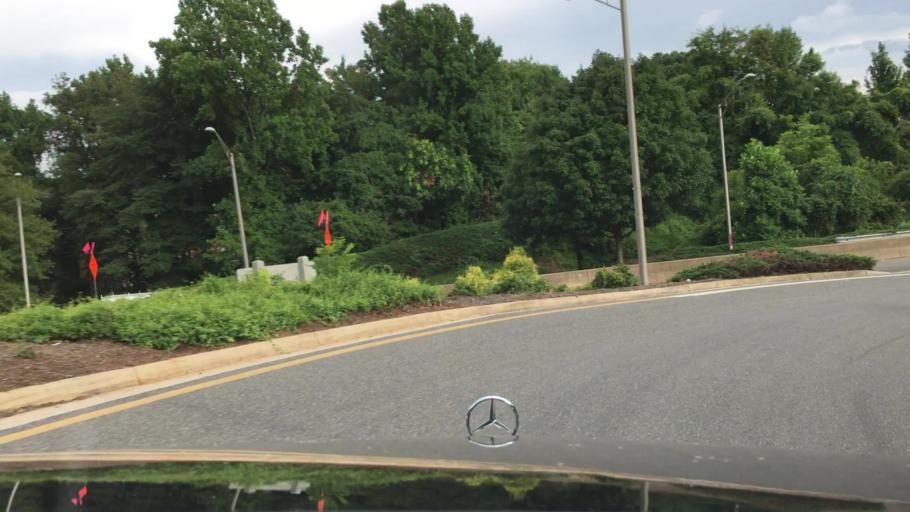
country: US
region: Virginia
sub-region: City of Lynchburg
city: West Lynchburg
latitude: 37.3869
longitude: -79.1675
